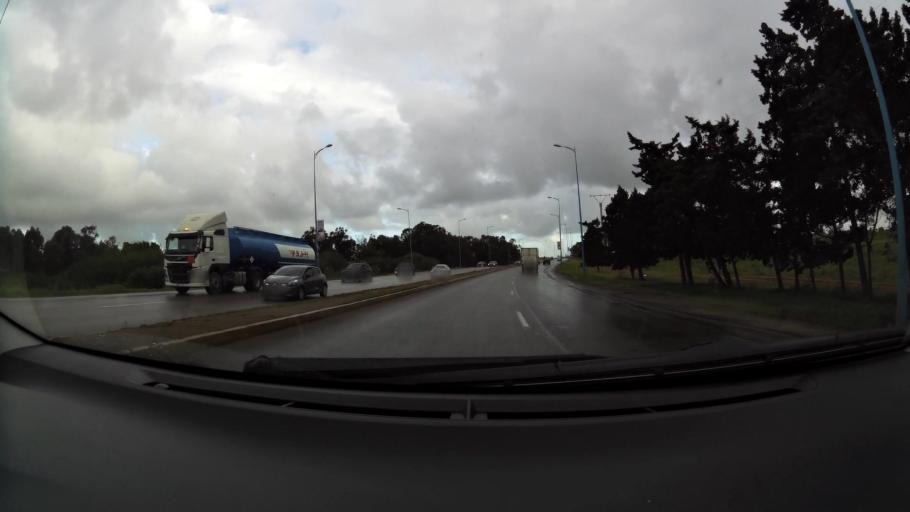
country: MA
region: Grand Casablanca
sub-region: Mohammedia
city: Mohammedia
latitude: 33.6727
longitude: -7.4070
